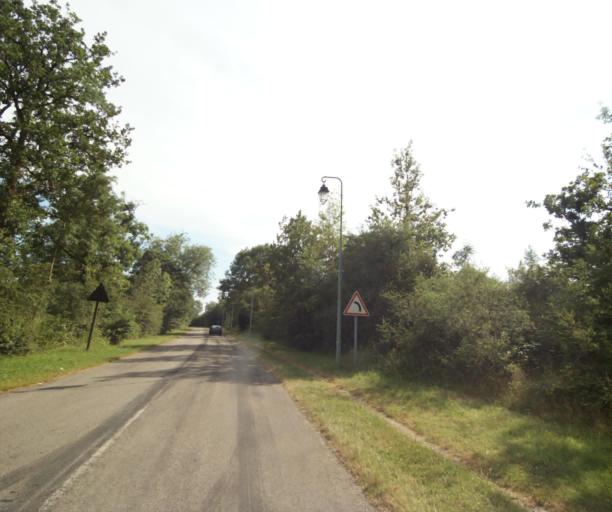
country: FR
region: Ile-de-France
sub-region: Departement de Seine-et-Marne
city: Acheres-la-Foret
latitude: 48.3588
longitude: 2.5628
